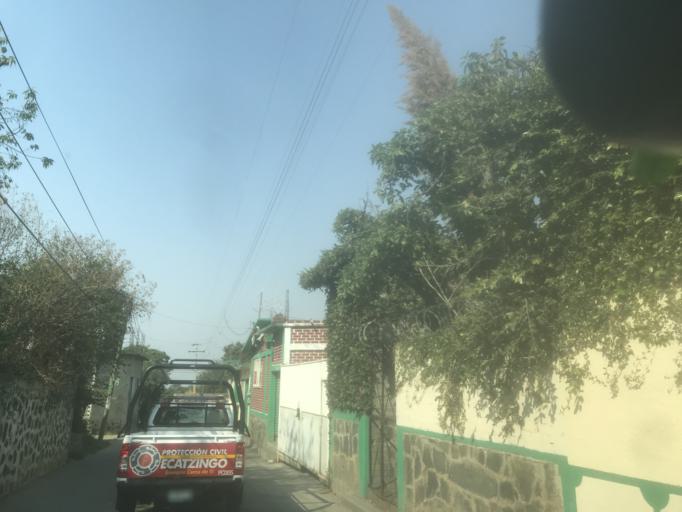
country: MX
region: Morelos
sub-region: Yecapixtla
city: Texcala
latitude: 18.9331
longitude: -98.7970
